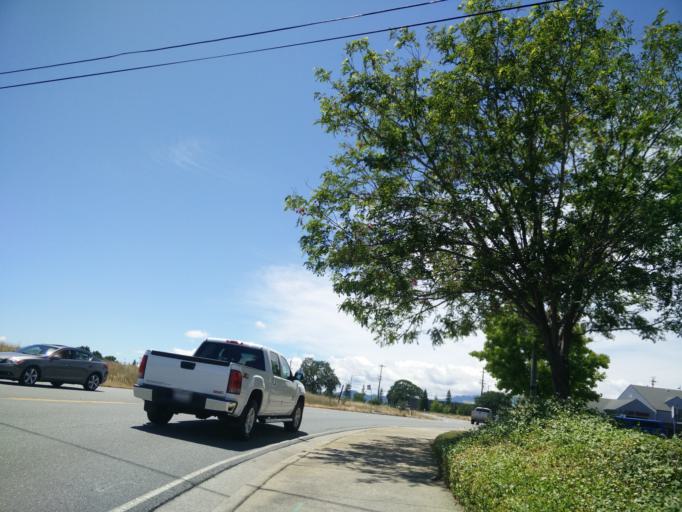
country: US
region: California
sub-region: Shasta County
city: Redding
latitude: 40.6092
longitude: -122.3743
